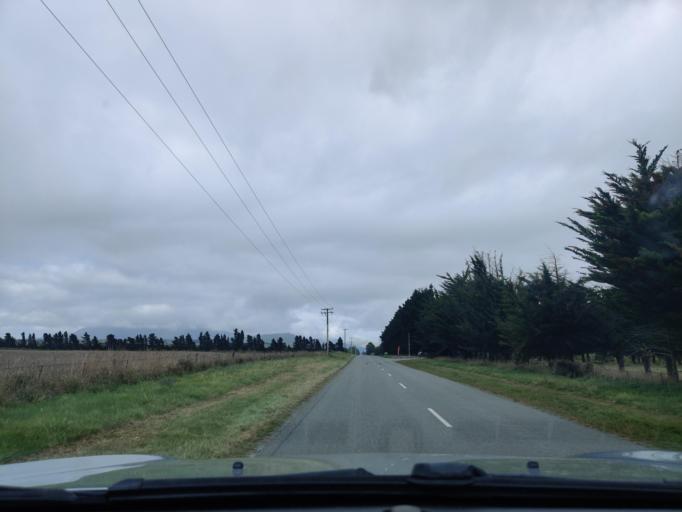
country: NZ
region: Canterbury
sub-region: Hurunui District
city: Amberley
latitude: -43.0770
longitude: 172.7183
